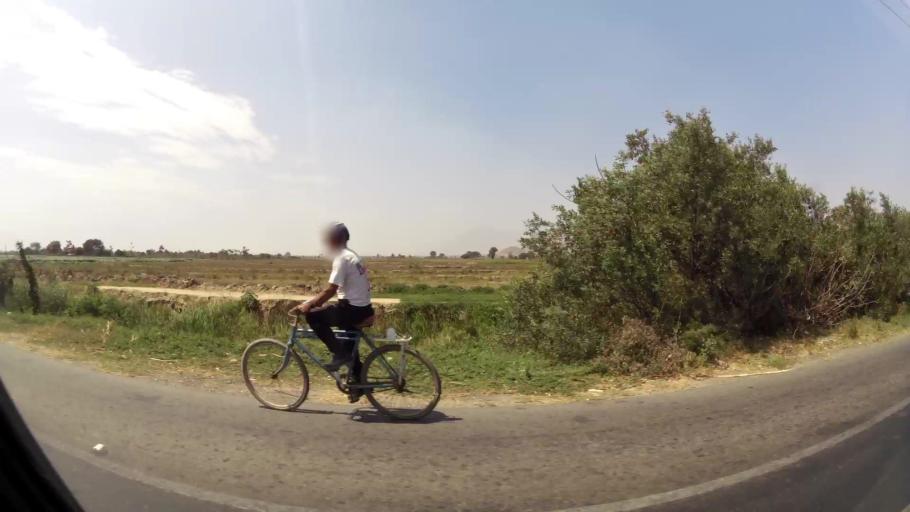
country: PE
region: La Libertad
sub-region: Chepen
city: Chepen
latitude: -7.1963
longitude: -79.4290
